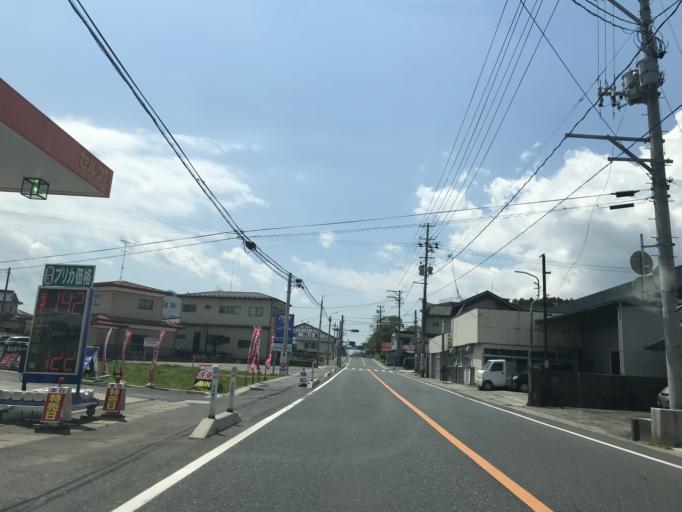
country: JP
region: Miyagi
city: Wakuya
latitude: 38.4810
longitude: 141.0978
